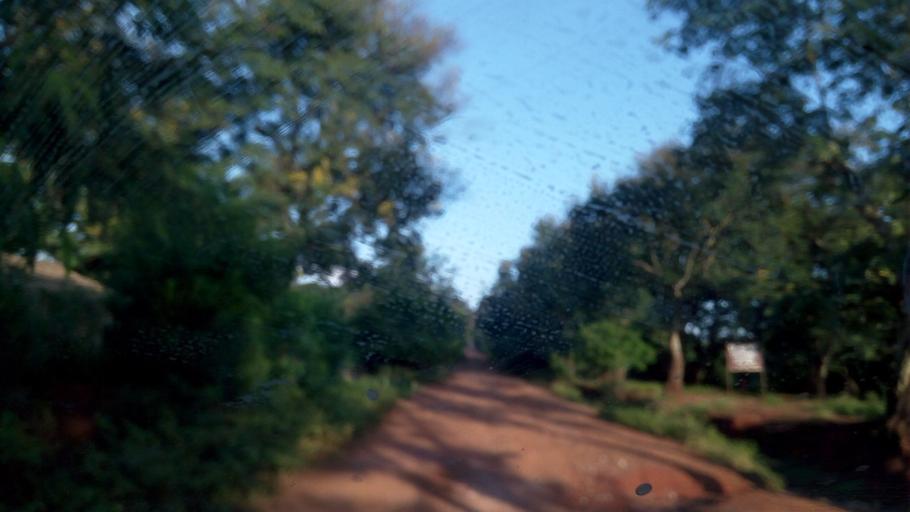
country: BI
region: Bururi
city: Rumonge
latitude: -4.2005
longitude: 29.0374
